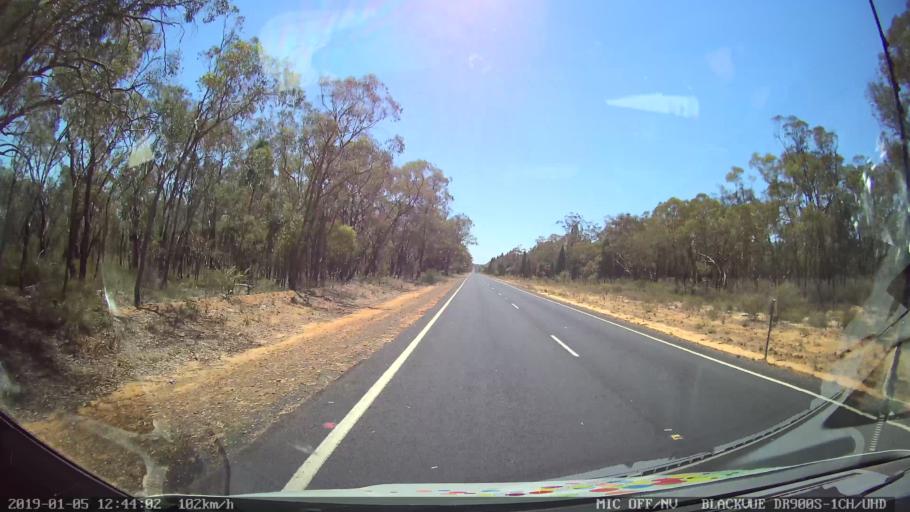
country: AU
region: New South Wales
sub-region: Warrumbungle Shire
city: Coonabarabran
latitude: -31.1418
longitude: 149.5320
